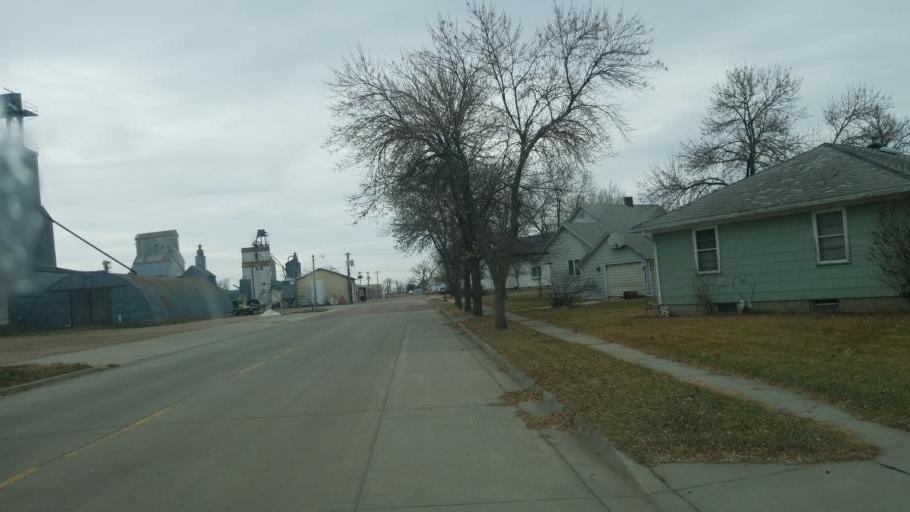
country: US
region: South Dakota
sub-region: Hutchinson County
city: Parkston
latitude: 43.2227
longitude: -97.9635
